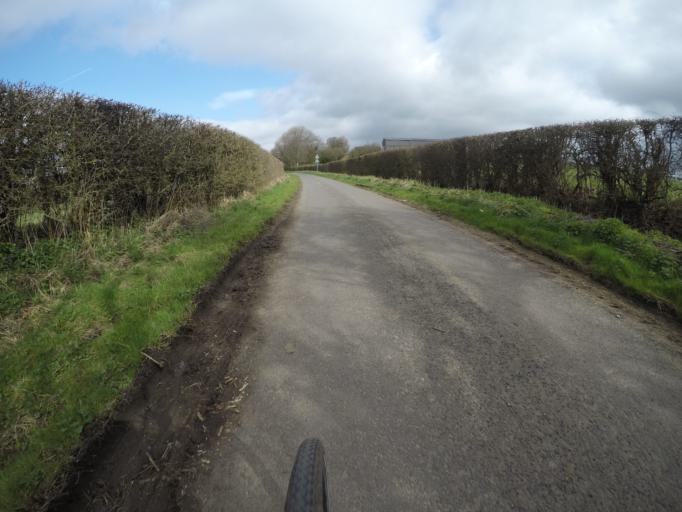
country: GB
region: Scotland
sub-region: North Ayrshire
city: Springside
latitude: 55.6482
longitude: -4.6181
